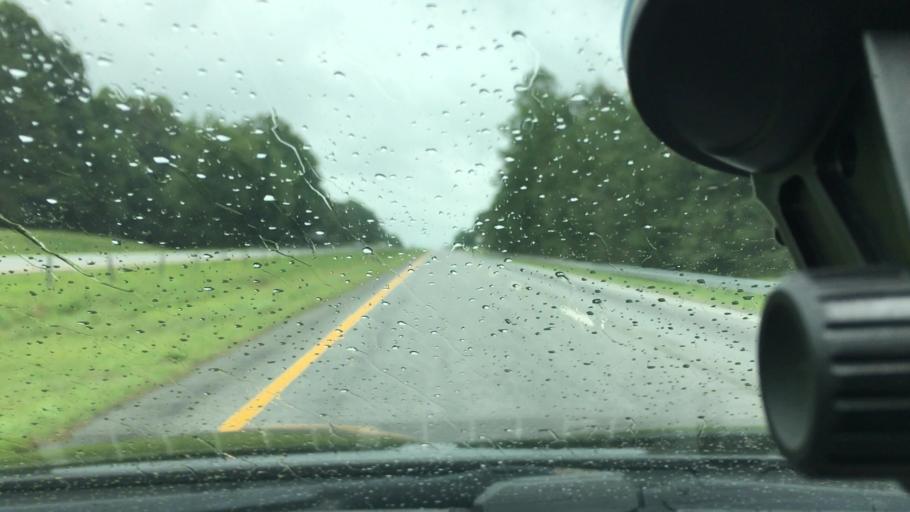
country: US
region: North Carolina
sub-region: Rutherford County
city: Forest City
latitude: 35.3025
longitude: -81.7657
